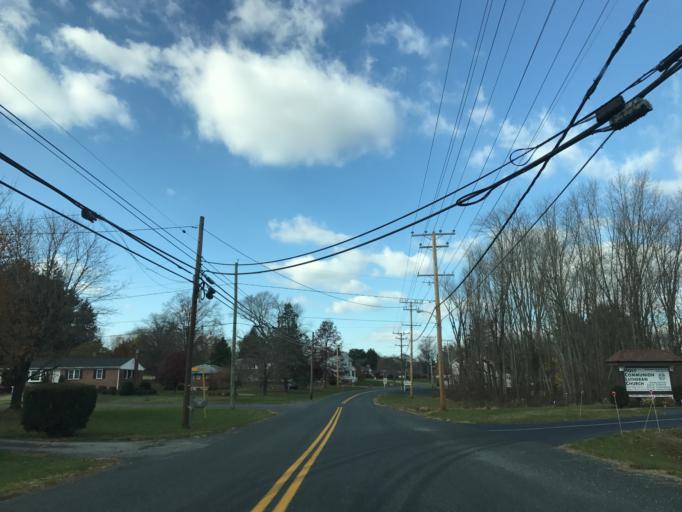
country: US
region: Maryland
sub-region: Harford County
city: Fallston
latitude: 39.5063
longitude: -76.4040
